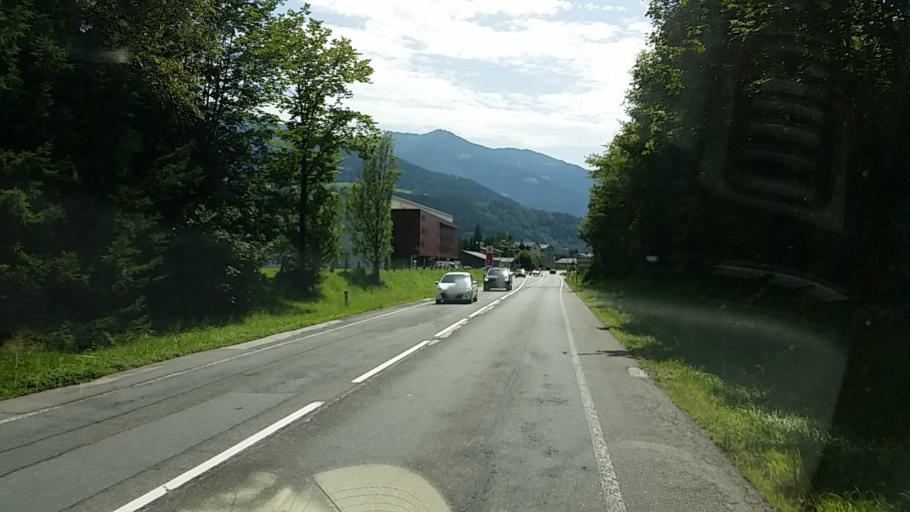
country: AT
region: Salzburg
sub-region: Politischer Bezirk Sankt Johann im Pongau
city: Bischofshofen
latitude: 47.4315
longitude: 13.2116
